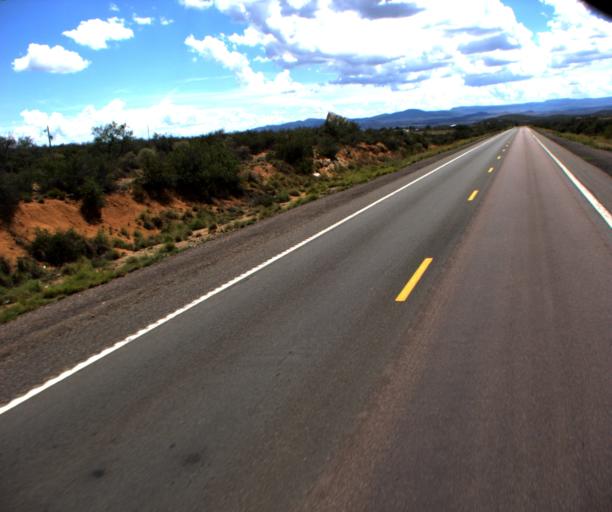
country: US
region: Arizona
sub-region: Yavapai County
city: Dewey-Humboldt
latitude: 34.5420
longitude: -112.1523
